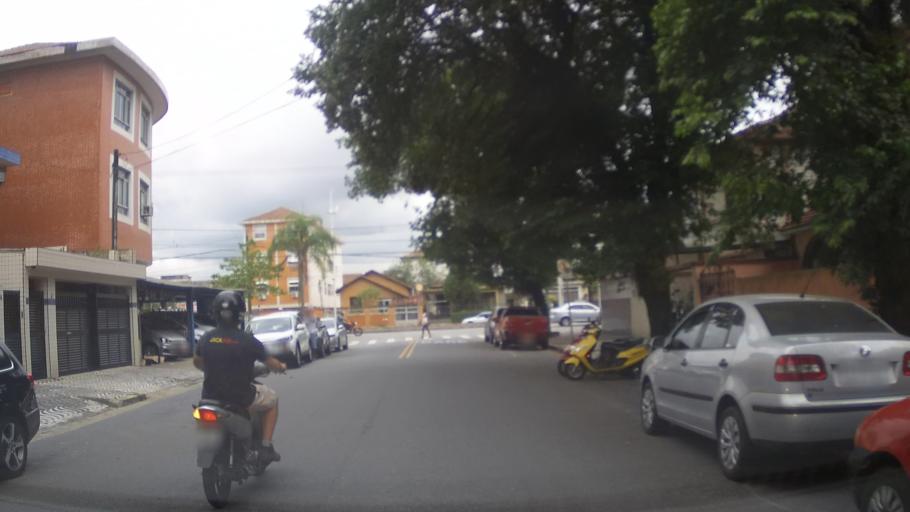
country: BR
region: Sao Paulo
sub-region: Santos
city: Santos
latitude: -23.9681
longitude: -46.3074
